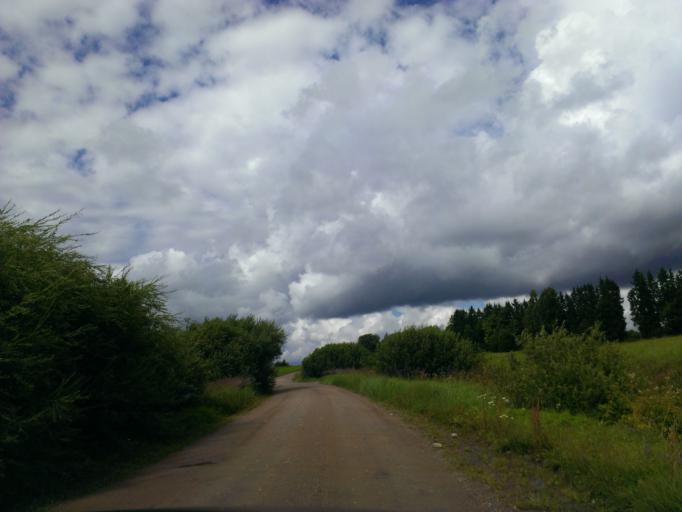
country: LV
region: Ligatne
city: Ligatne
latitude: 57.2211
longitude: 25.0068
